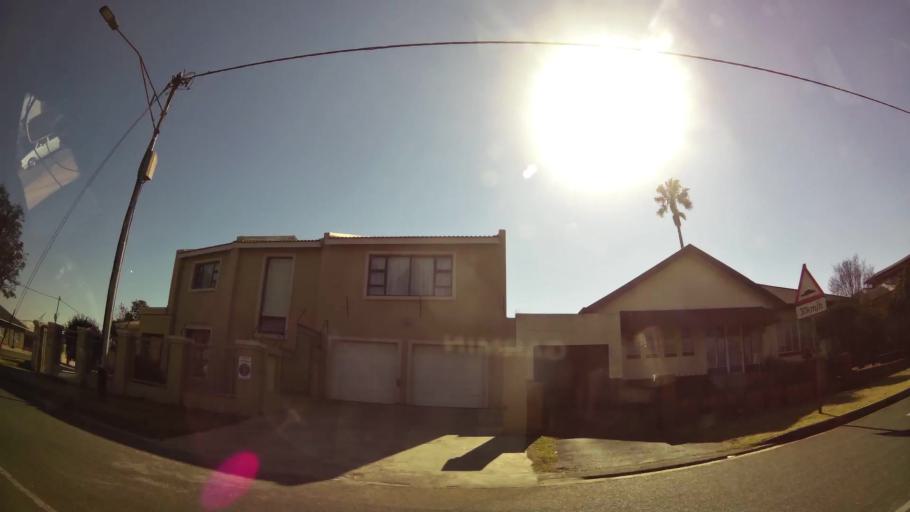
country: ZA
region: Gauteng
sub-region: City of Johannesburg Metropolitan Municipality
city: Johannesburg
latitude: -26.1914
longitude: 27.9843
